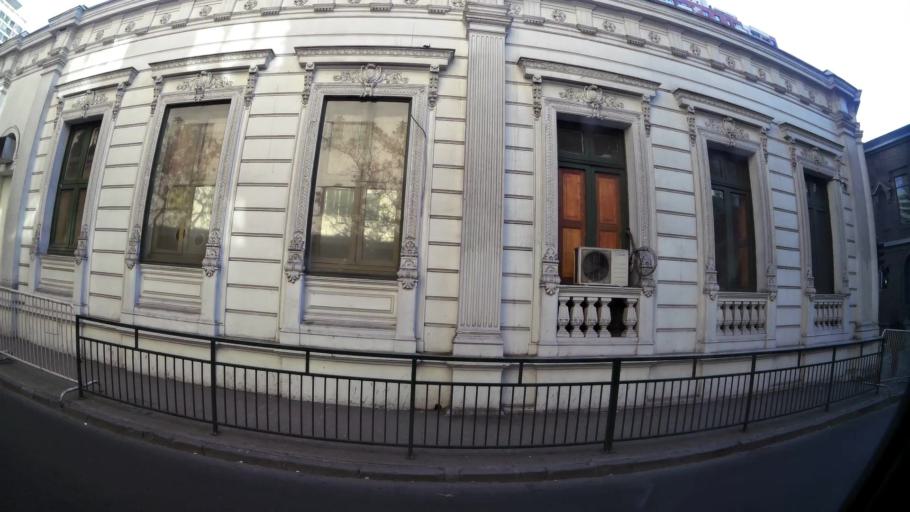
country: CL
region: Santiago Metropolitan
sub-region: Provincia de Santiago
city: Santiago
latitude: -33.4359
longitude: -70.6473
